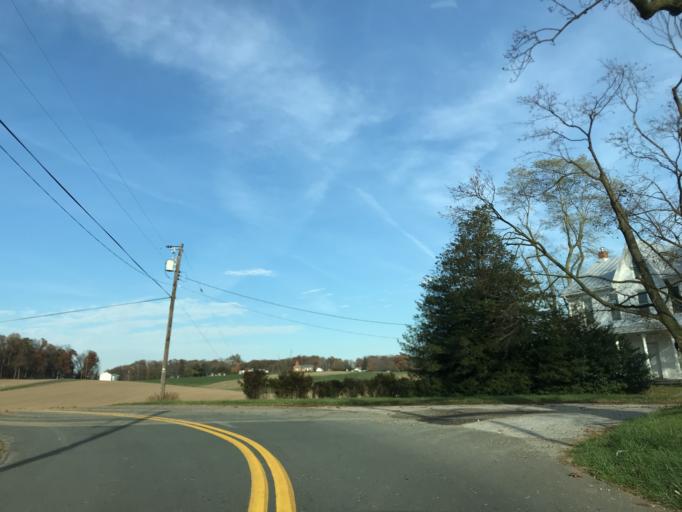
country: US
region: Maryland
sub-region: Carroll County
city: Hampstead
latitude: 39.5694
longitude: -76.7858
